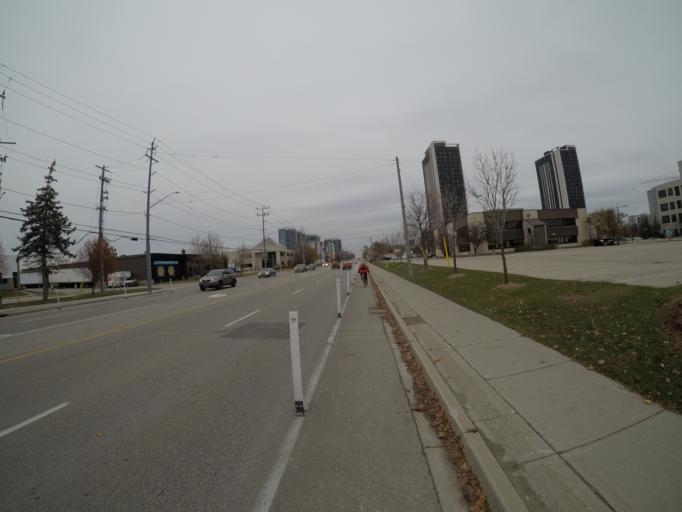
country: CA
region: Ontario
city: Waterloo
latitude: 43.4762
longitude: -80.5418
